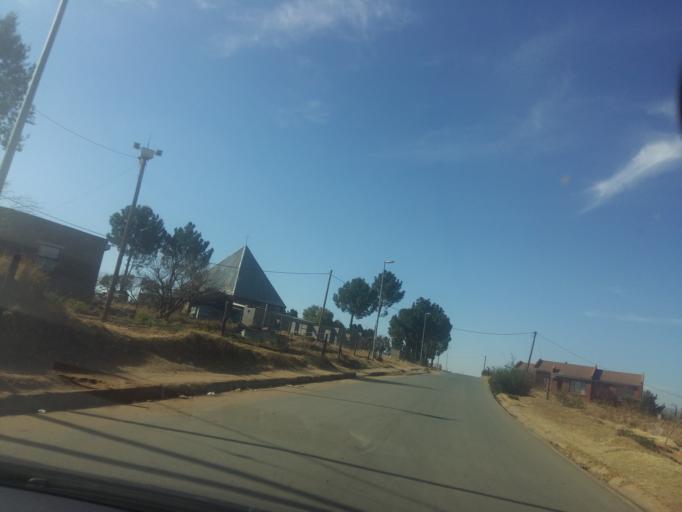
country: LS
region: Maseru
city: Maseru
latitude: -29.3918
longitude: 27.5245
